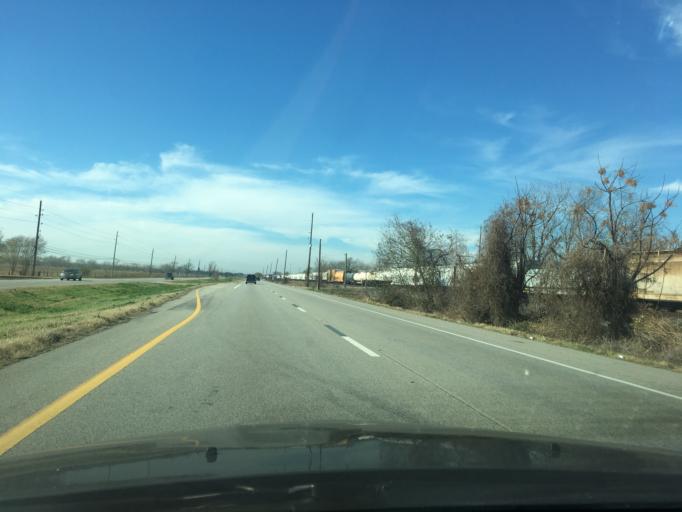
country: US
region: Texas
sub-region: Fort Bend County
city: New Territory
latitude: 29.6005
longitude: -95.6981
